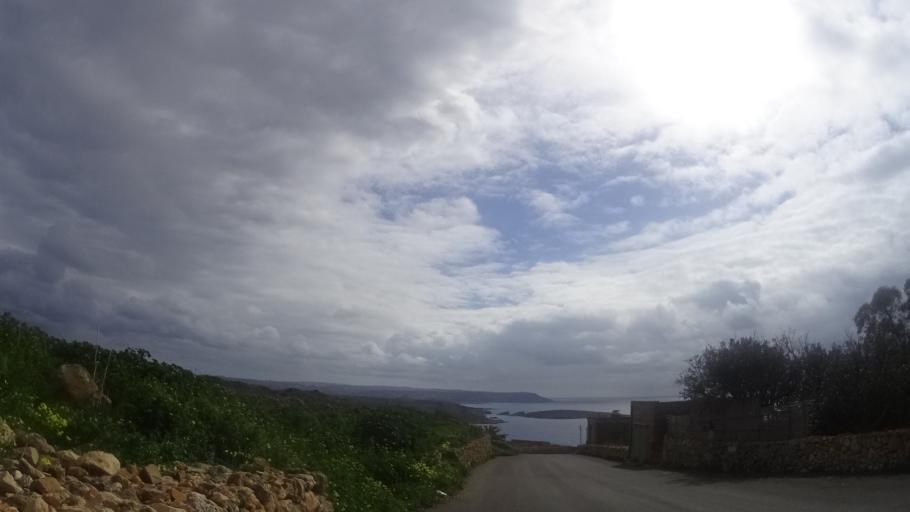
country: MT
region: Il-Qala
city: Qala
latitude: 36.0331
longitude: 14.3215
